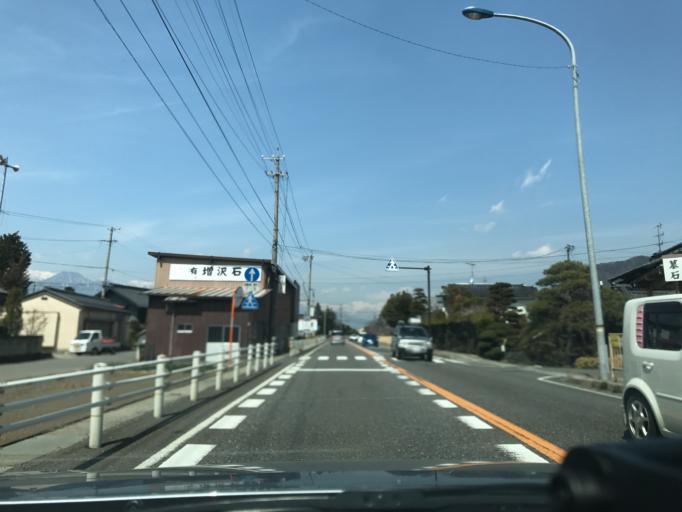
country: JP
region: Nagano
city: Toyoshina
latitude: 36.2932
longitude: 137.9429
